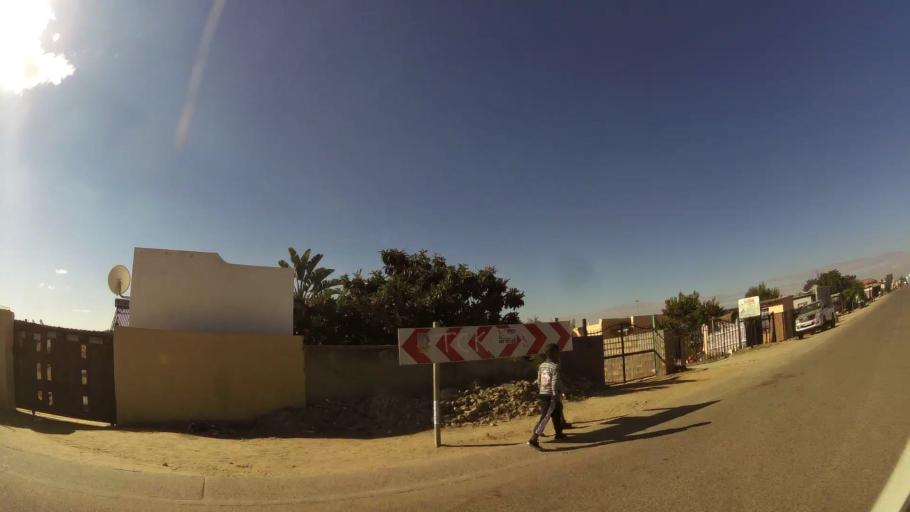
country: ZA
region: Gauteng
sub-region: City of Johannesburg Metropolitan Municipality
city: Diepsloot
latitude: -25.9129
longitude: 28.0890
